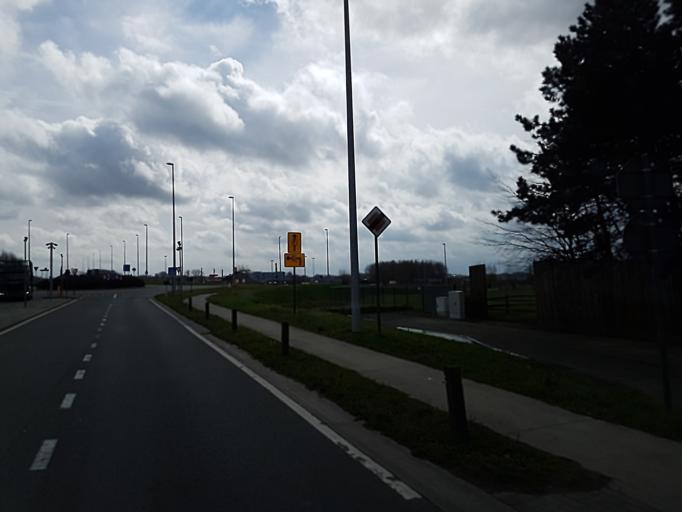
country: BE
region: Flanders
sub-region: Provincie Oost-Vlaanderen
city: Kruishoutem
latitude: 50.9173
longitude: 3.4911
